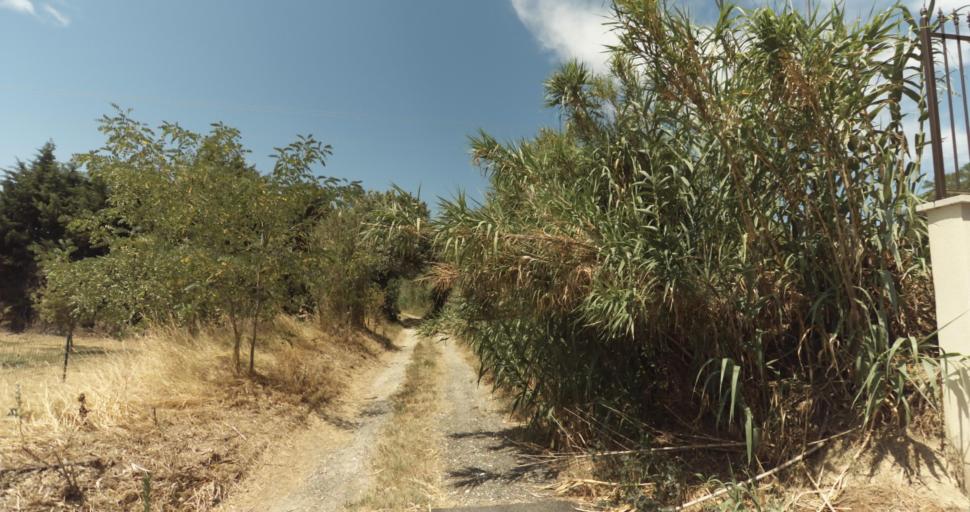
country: FR
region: Provence-Alpes-Cote d'Azur
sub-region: Departement du Vaucluse
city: Monteux
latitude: 44.0519
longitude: 5.0199
